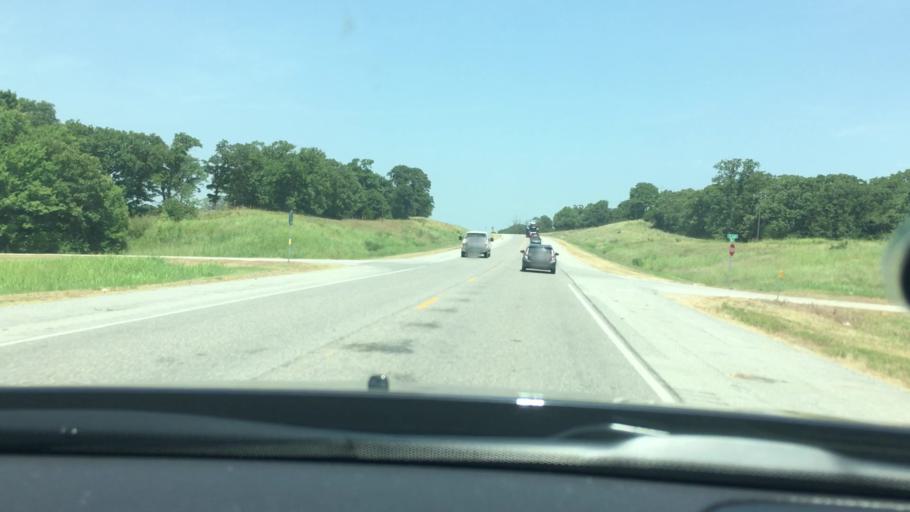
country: US
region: Oklahoma
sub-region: Coal County
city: Coalgate
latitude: 34.6060
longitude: -96.3757
